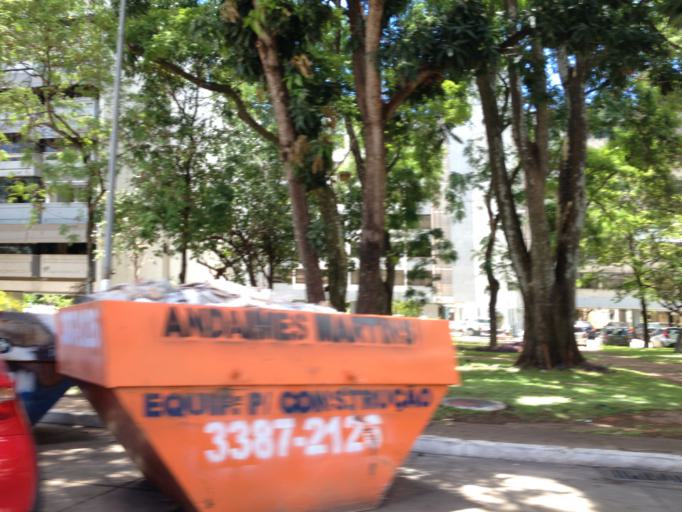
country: BR
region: Federal District
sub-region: Brasilia
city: Brasilia
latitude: -15.8216
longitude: -47.9178
